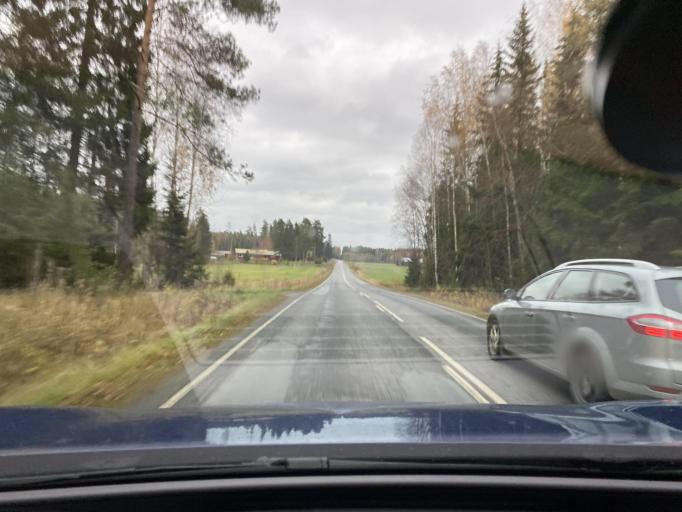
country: FI
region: Satakunta
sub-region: Pori
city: Huittinen
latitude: 61.1250
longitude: 22.5870
